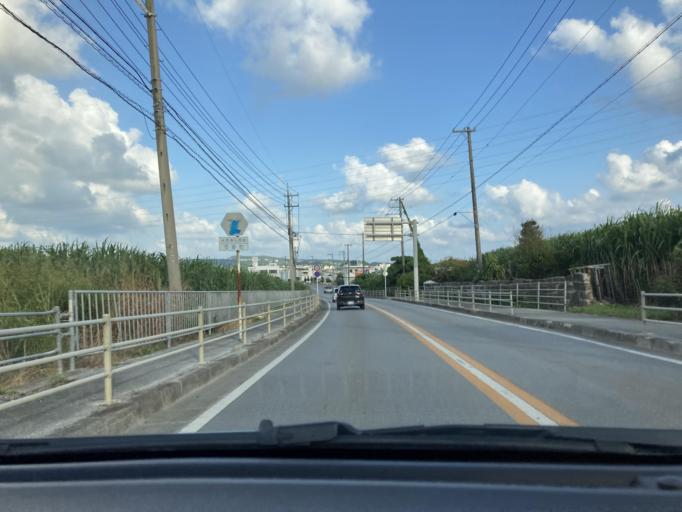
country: JP
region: Okinawa
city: Tomigusuku
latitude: 26.1498
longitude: 127.7116
